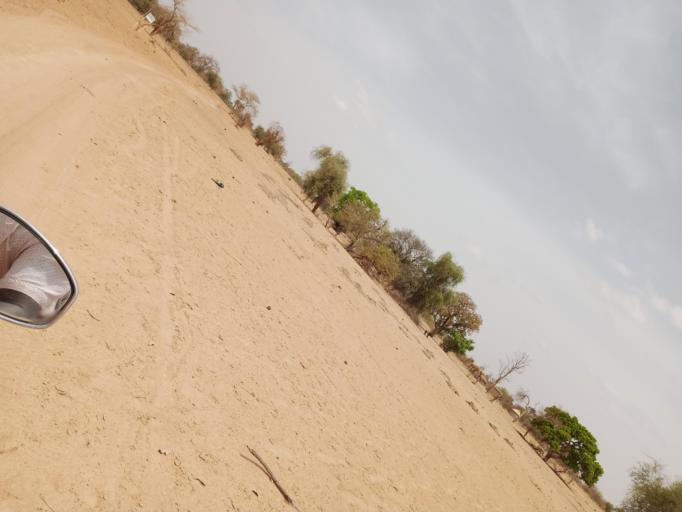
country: BF
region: Est
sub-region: Gnagna Province
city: Bogande
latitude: 13.0974
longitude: -0.0455
